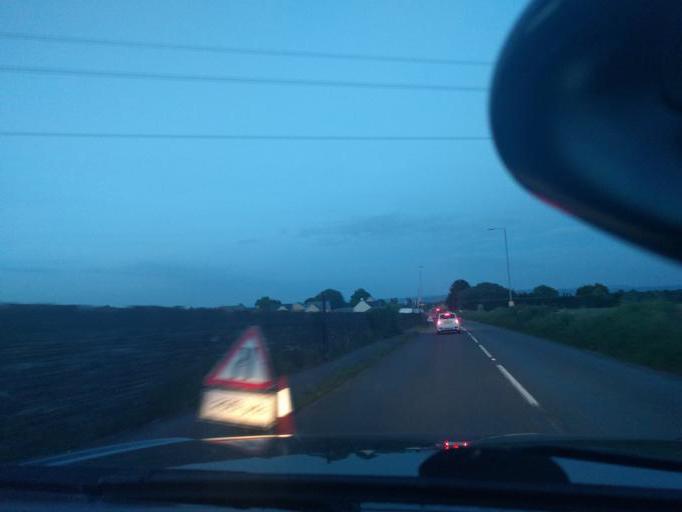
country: GB
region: England
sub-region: Wiltshire
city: Neston
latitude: 51.4322
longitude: -2.2196
